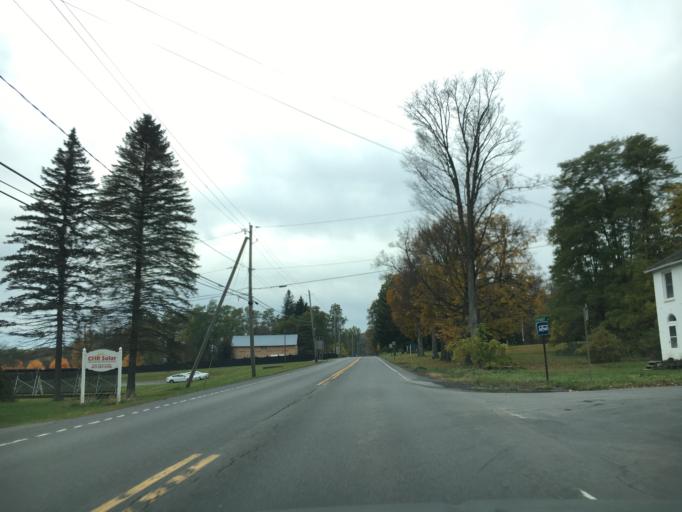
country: US
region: New York
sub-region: Otsego County
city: Cooperstown
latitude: 42.6442
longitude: -74.9650
